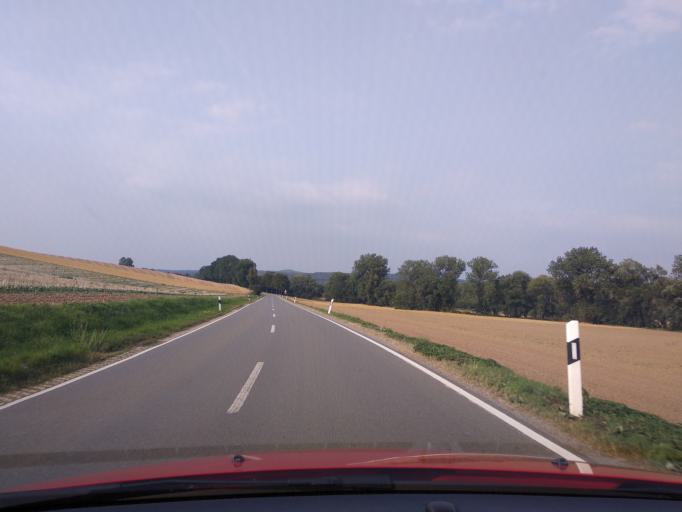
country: DE
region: Hesse
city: Liebenau
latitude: 51.4483
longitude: 9.3069
